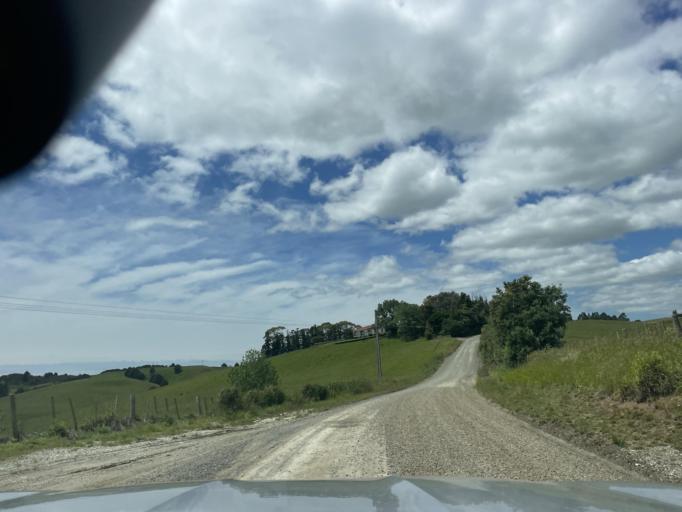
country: NZ
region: Auckland
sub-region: Auckland
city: Wellsford
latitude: -36.1576
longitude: 174.5284
